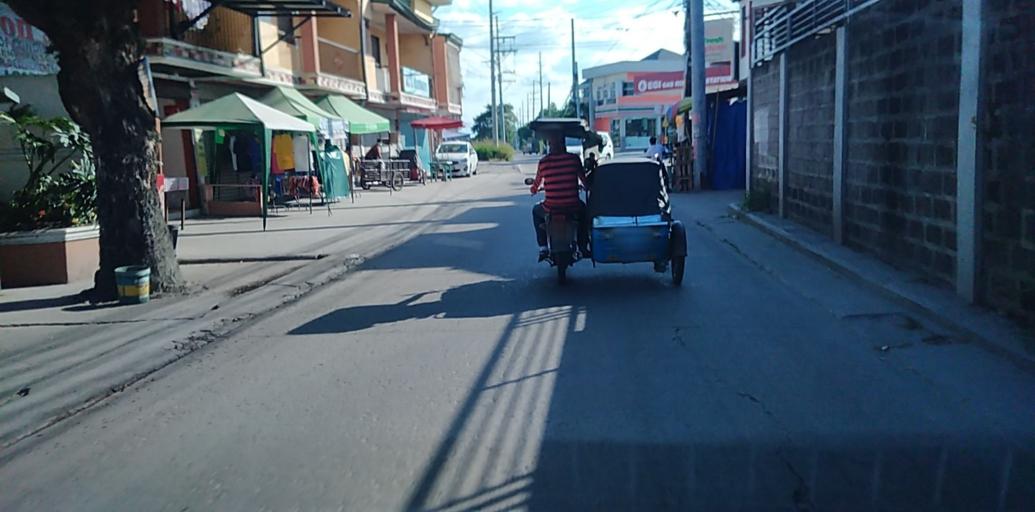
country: PH
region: Central Luzon
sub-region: Province of Pampanga
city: Acli
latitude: 15.1129
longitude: 120.6330
